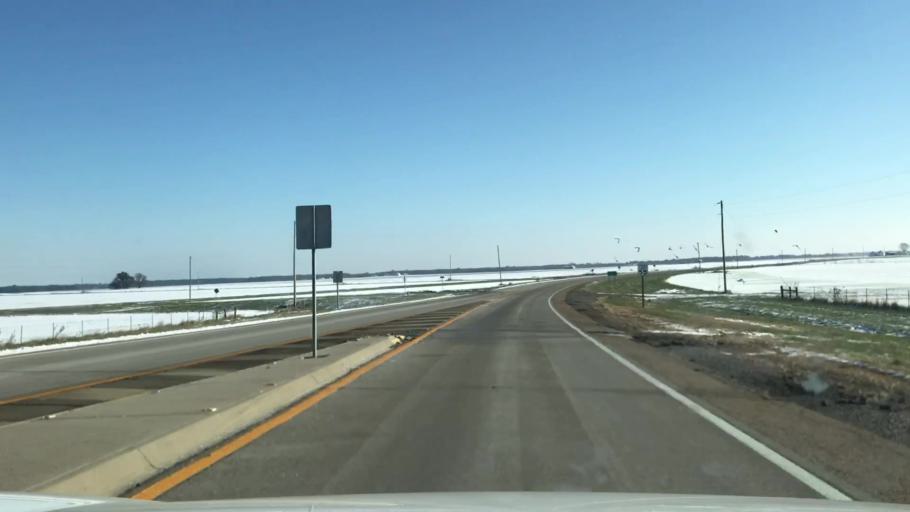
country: US
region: Illinois
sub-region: Washington County
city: Okawville
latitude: 38.4417
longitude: -89.5265
